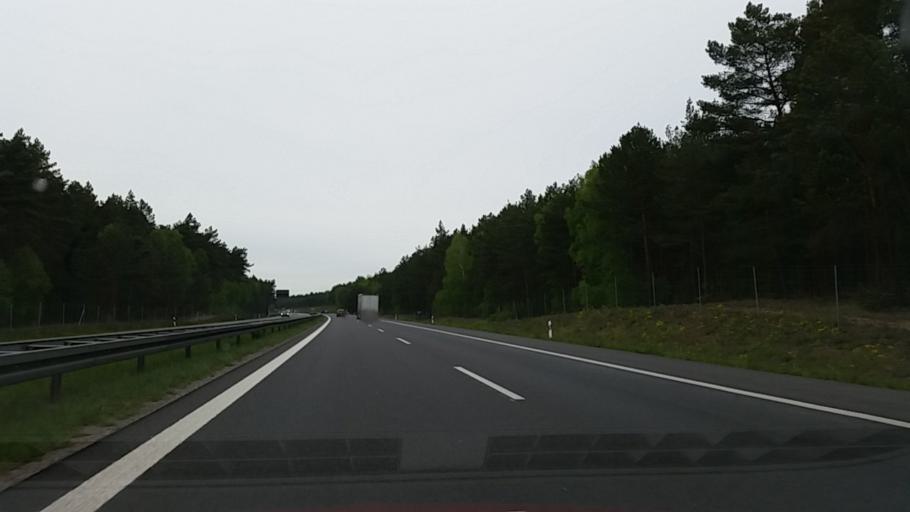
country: DE
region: Brandenburg
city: Wittstock
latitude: 53.0829
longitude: 12.5208
